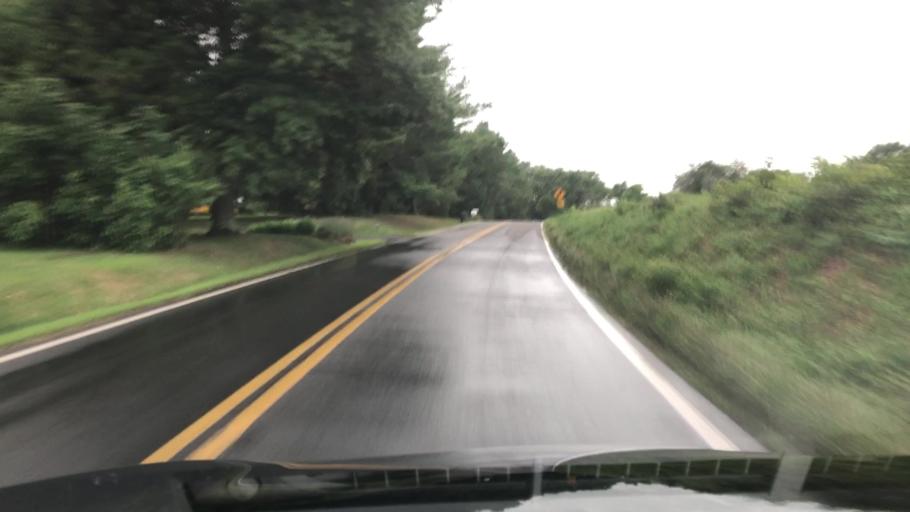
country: US
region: Virginia
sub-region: Prince William County
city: Nokesville
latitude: 38.5840
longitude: -77.6098
